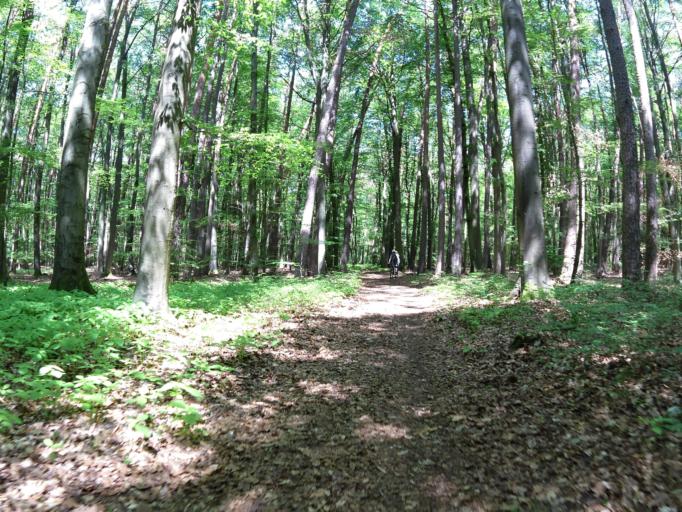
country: DE
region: Bavaria
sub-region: Regierungsbezirk Unterfranken
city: Theilheim
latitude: 49.7459
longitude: 10.0204
